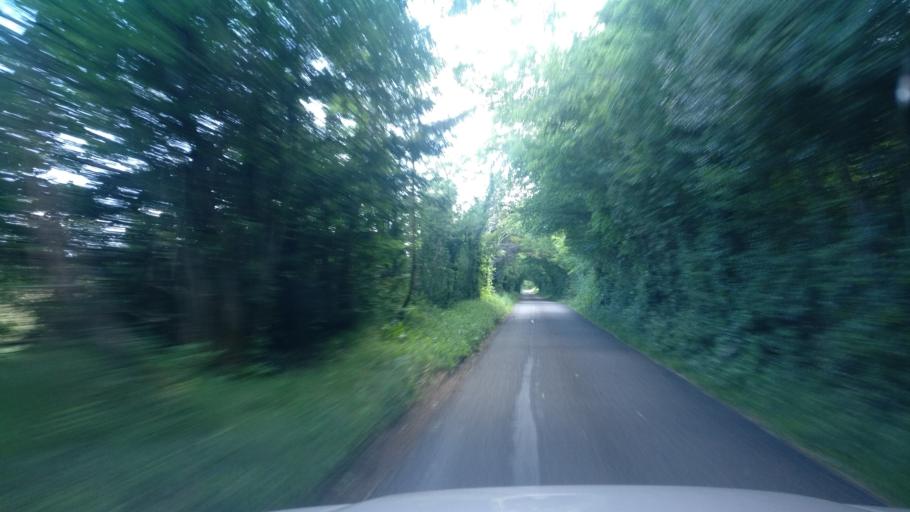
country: IE
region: Connaught
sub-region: County Galway
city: Ballinasloe
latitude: 53.2249
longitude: -8.1978
